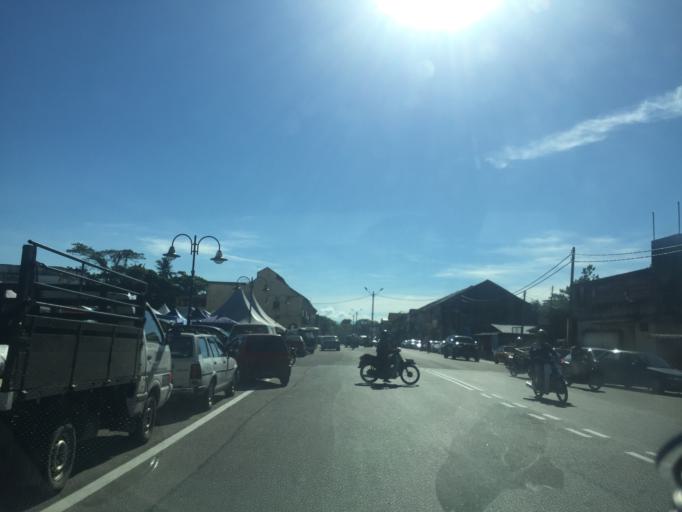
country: MY
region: Penang
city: Tasek Glugor
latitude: 5.5135
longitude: 100.5529
